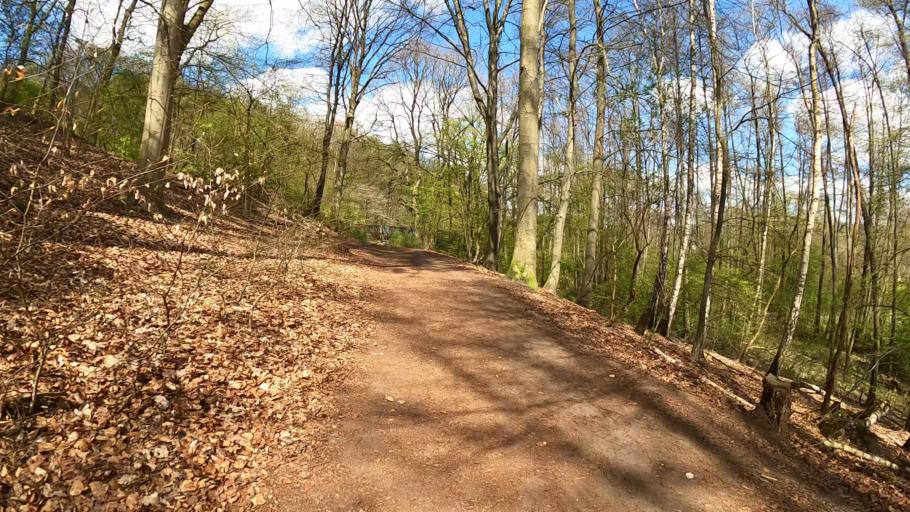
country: DE
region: Schleswig-Holstein
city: Wentorf bei Hamburg
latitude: 53.4996
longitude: 10.2396
